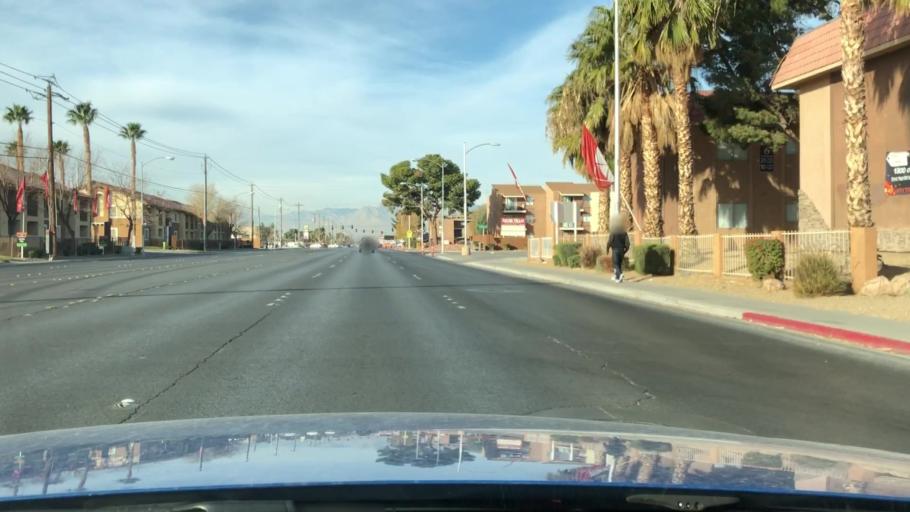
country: US
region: Nevada
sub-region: Clark County
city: North Las Vegas
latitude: 36.1958
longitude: -115.0950
